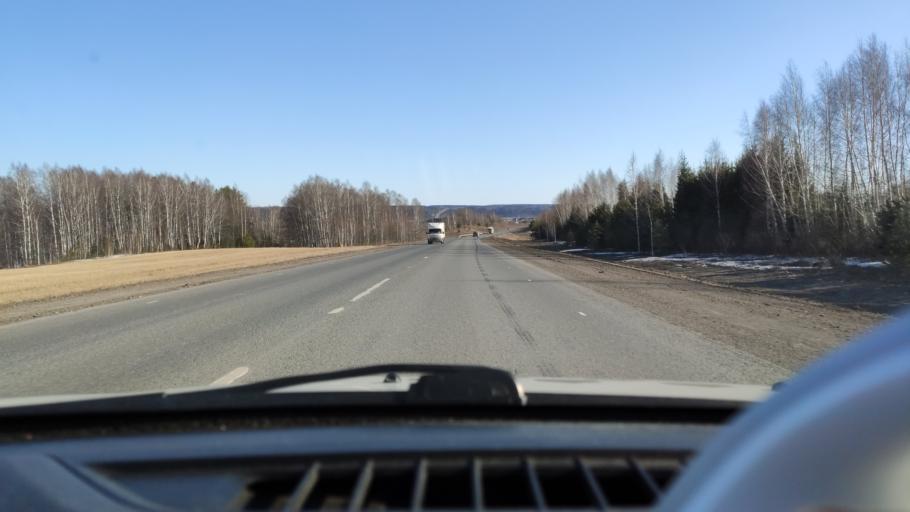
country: RU
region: Perm
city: Kungur
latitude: 57.3948
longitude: 56.9004
